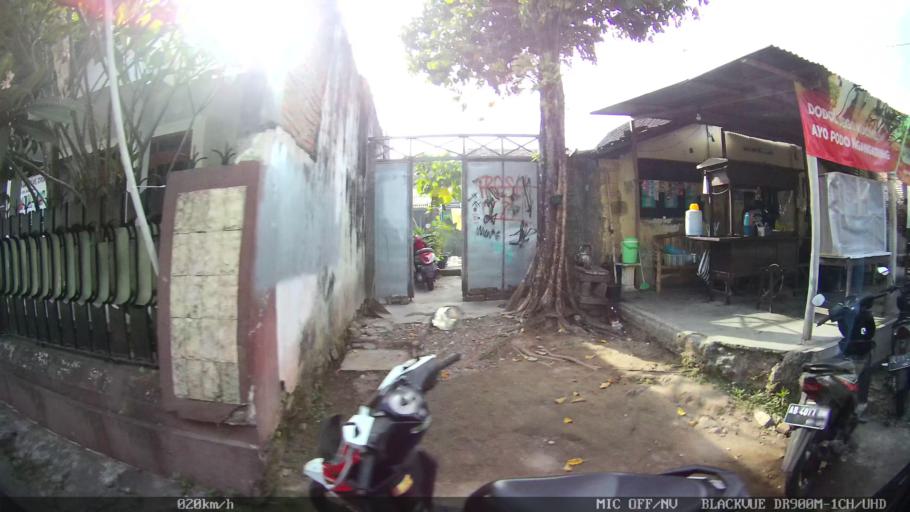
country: ID
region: Daerah Istimewa Yogyakarta
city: Kasihan
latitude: -7.8200
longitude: 110.3650
